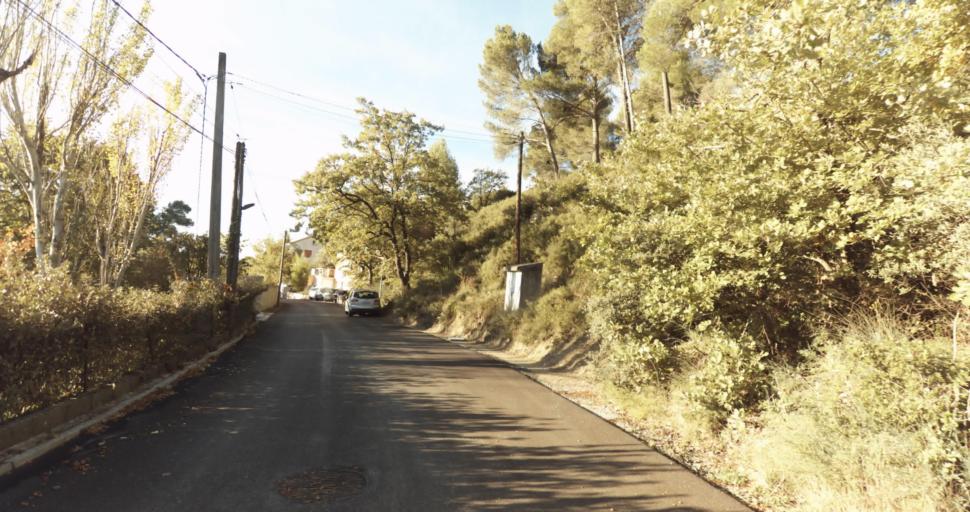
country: FR
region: Provence-Alpes-Cote d'Azur
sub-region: Departement des Bouches-du-Rhone
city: Venelles
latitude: 43.6053
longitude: 5.4794
